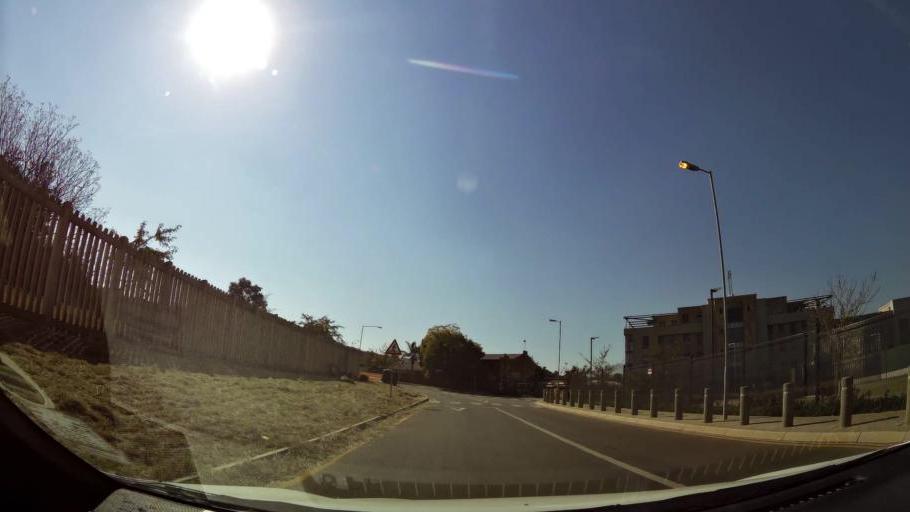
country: ZA
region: Gauteng
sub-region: City of Tshwane Metropolitan Municipality
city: Pretoria
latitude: -25.7768
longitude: 28.2682
